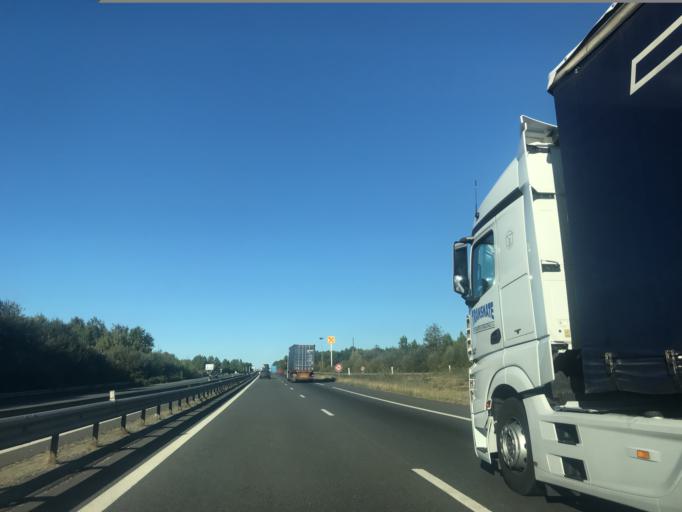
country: FR
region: Aquitaine
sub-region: Departement de la Gironde
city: Laruscade
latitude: 45.1841
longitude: -0.3206
